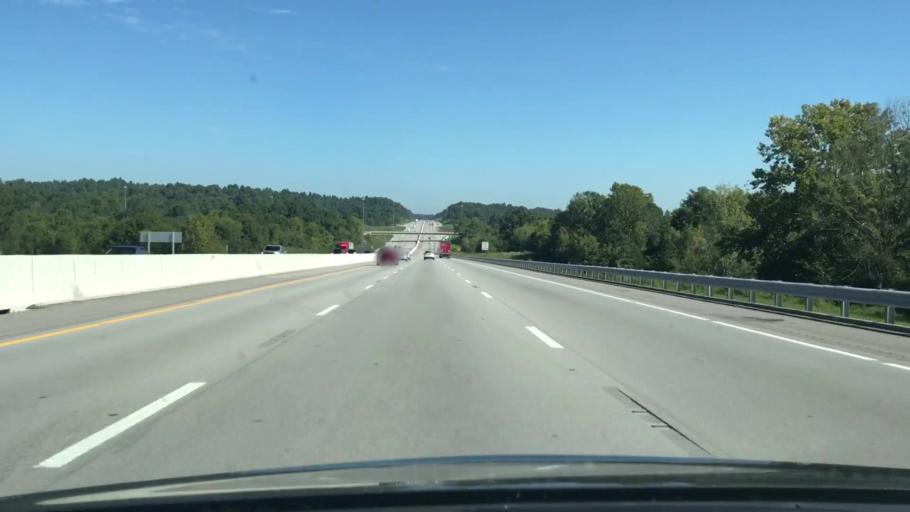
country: US
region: Kentucky
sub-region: Hart County
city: Munfordville
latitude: 37.3726
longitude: -85.8907
